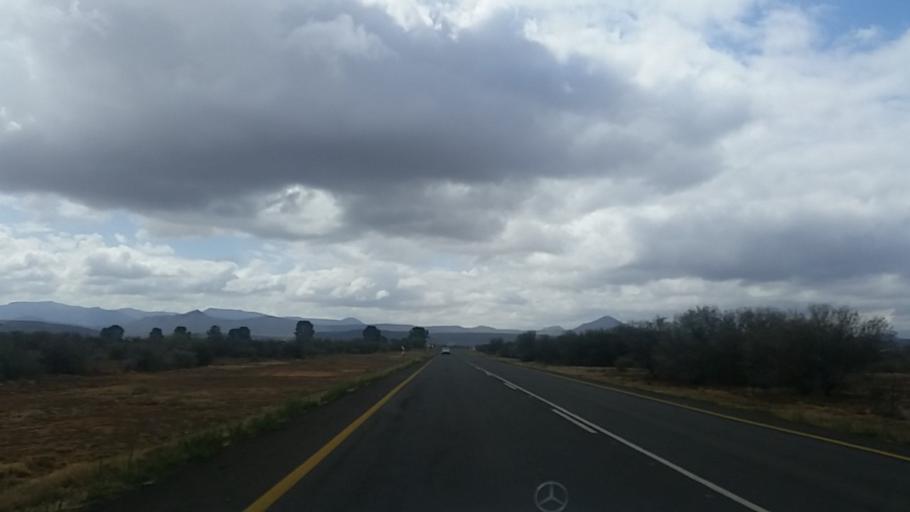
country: ZA
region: Eastern Cape
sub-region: Cacadu District Municipality
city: Graaff-Reinet
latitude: -32.1981
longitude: 24.5538
